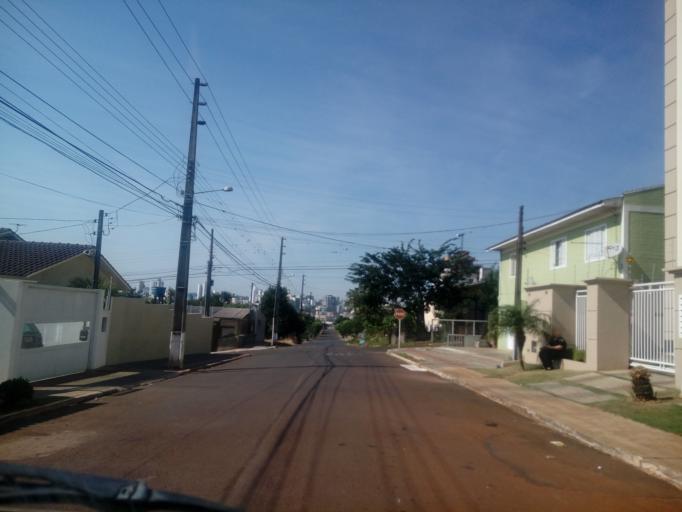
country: BR
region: Santa Catarina
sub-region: Chapeco
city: Chapeco
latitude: -27.0875
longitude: -52.6282
